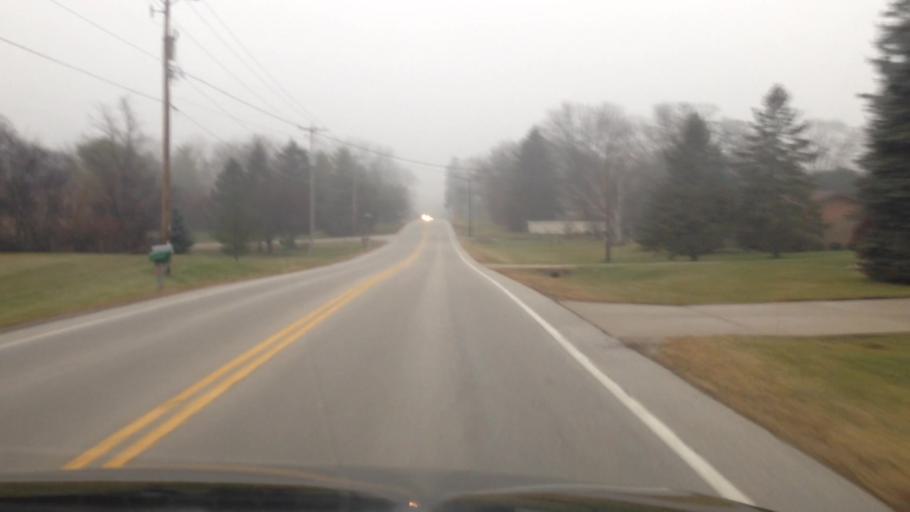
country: US
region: Wisconsin
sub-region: Milwaukee County
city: Hales Corners
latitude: 42.9179
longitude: -88.0780
